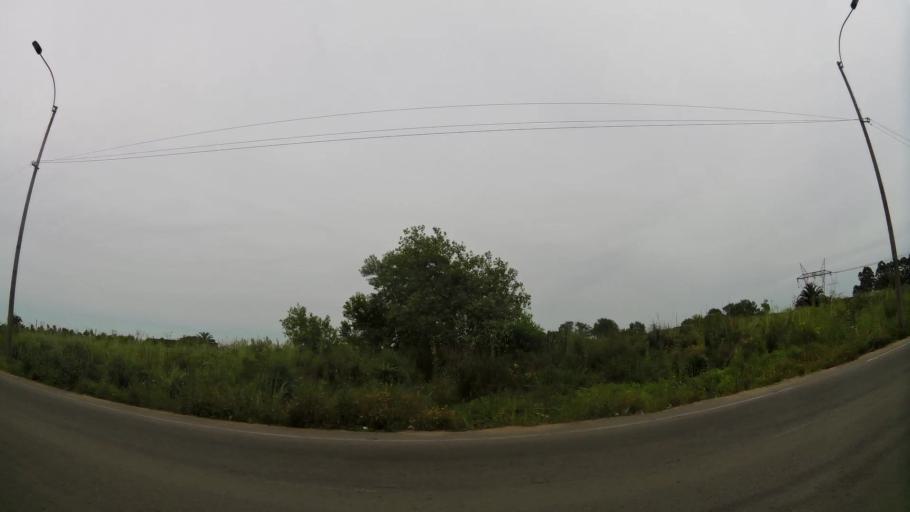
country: UY
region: Canelones
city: La Paz
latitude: -34.7778
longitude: -56.2253
